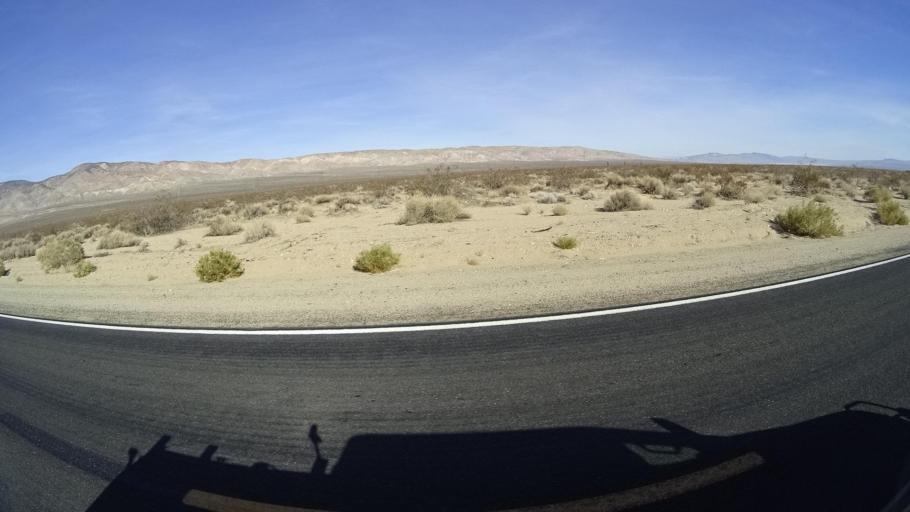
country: US
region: California
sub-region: Kern County
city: Mojave
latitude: 35.1250
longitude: -118.1339
